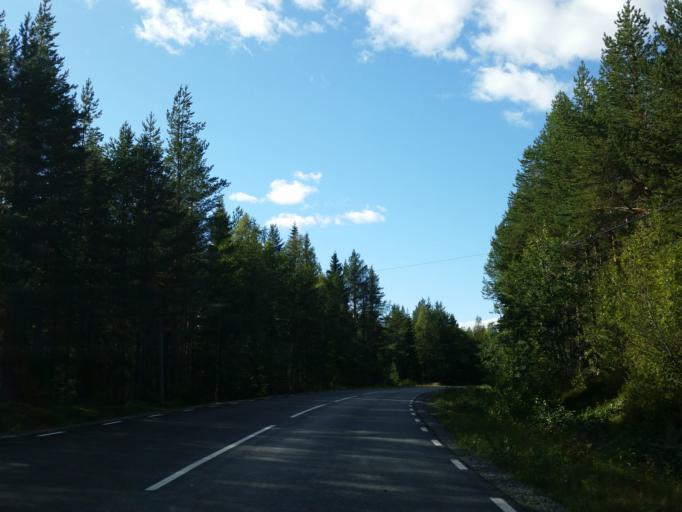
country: SE
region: Vaesterbotten
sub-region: Robertsfors Kommun
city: Robertsfors
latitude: 64.1602
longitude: 20.9425
